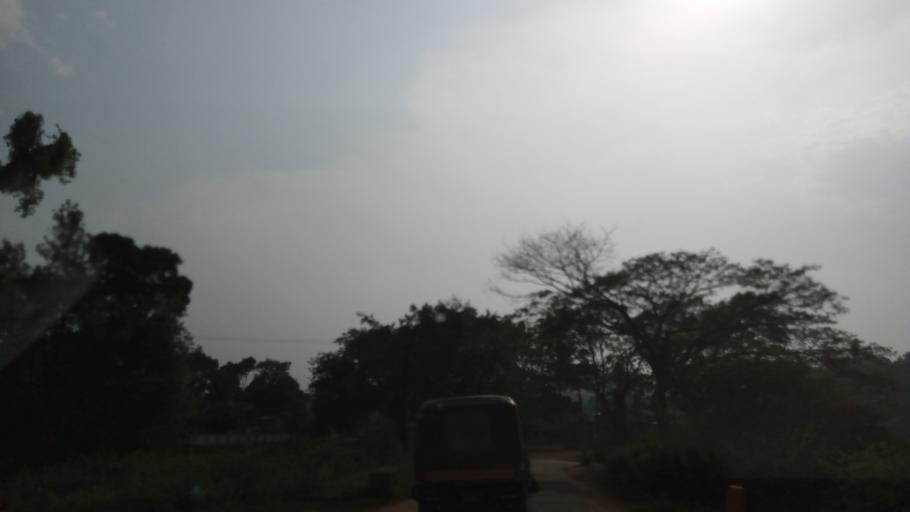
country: IN
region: Karnataka
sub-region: Chikmagalur
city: Mudigere
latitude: 13.0558
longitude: 75.6584
